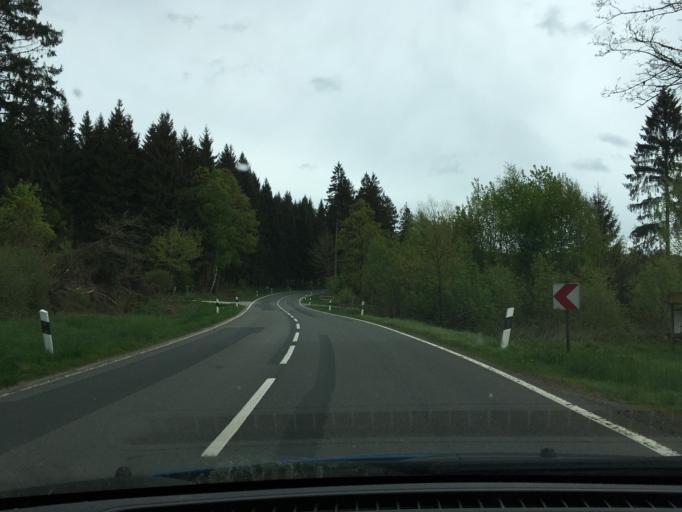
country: DE
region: Lower Saxony
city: Derental
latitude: 51.6889
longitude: 9.4756
